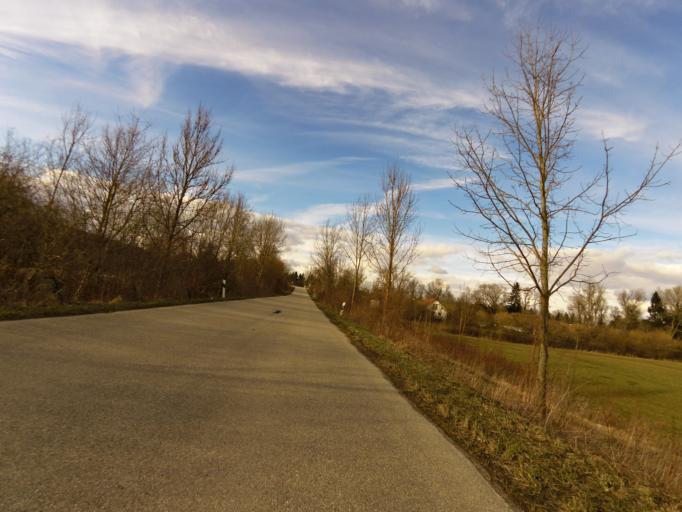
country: DE
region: Bavaria
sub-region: Upper Bavaria
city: Wang
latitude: 48.4887
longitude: 11.9885
